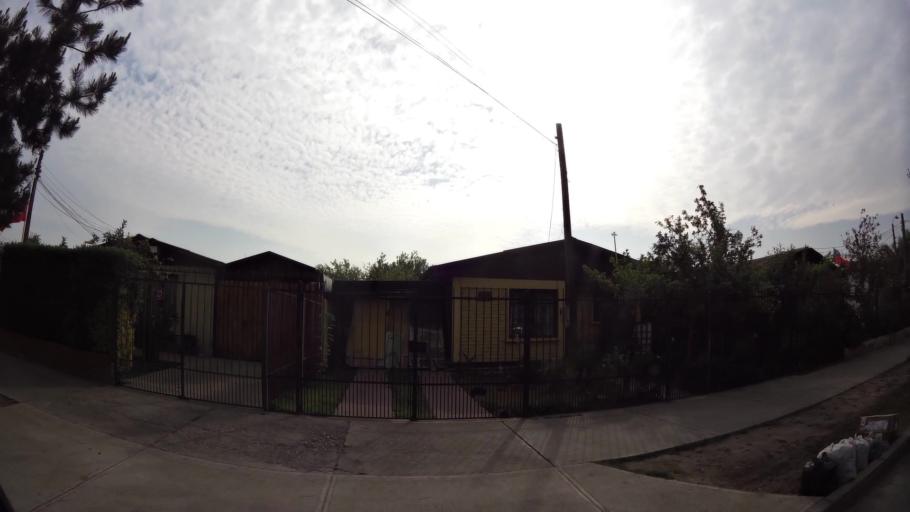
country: CL
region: Santiago Metropolitan
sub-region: Provincia de Santiago
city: Lo Prado
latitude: -33.5154
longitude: -70.7514
